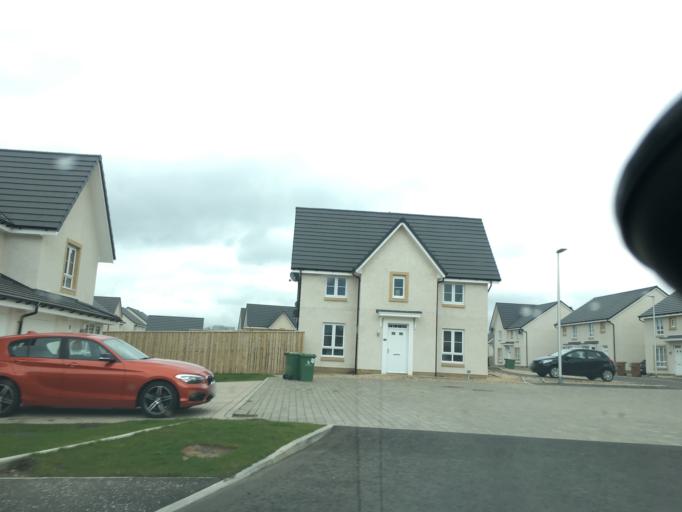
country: GB
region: Scotland
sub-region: Stirling
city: Bridge of Allan
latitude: 56.1356
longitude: -3.9601
